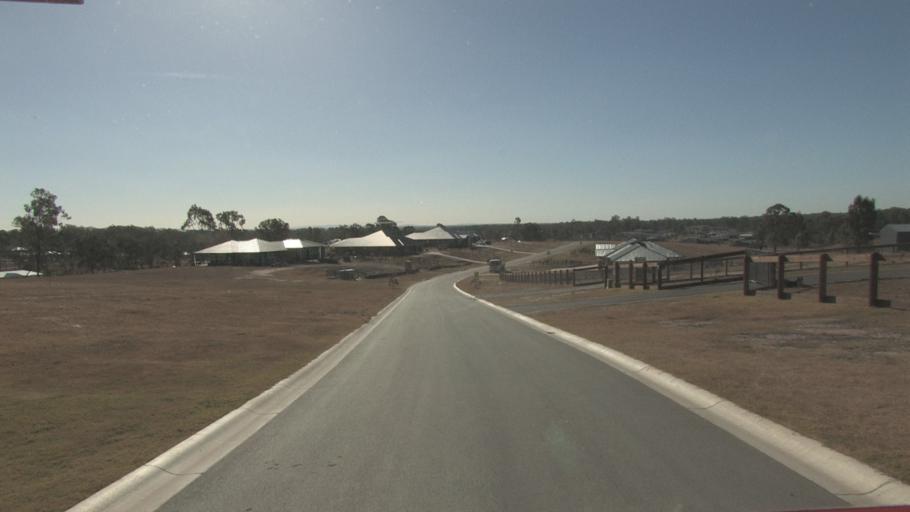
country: AU
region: Queensland
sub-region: Logan
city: Cedar Vale
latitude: -27.8766
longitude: 153.0469
